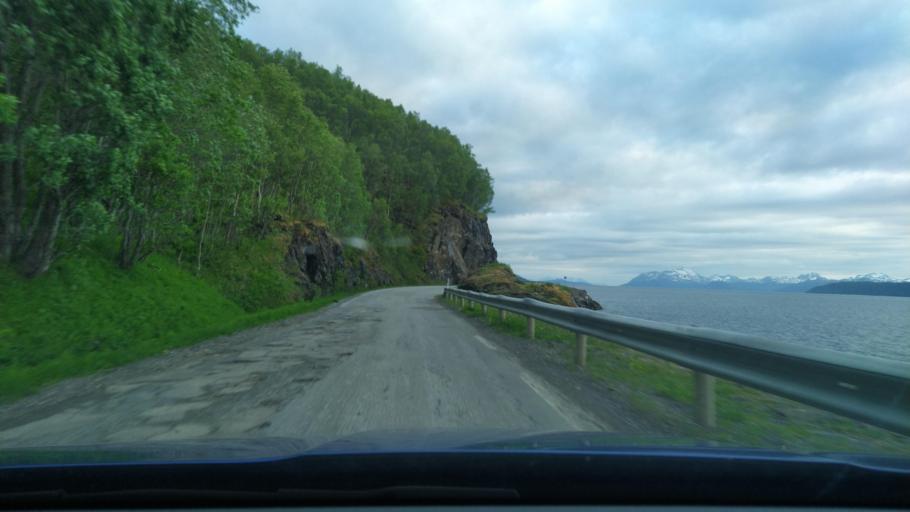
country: NO
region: Troms
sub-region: Lenvik
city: Finnsnes
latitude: 69.1462
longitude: 17.9332
